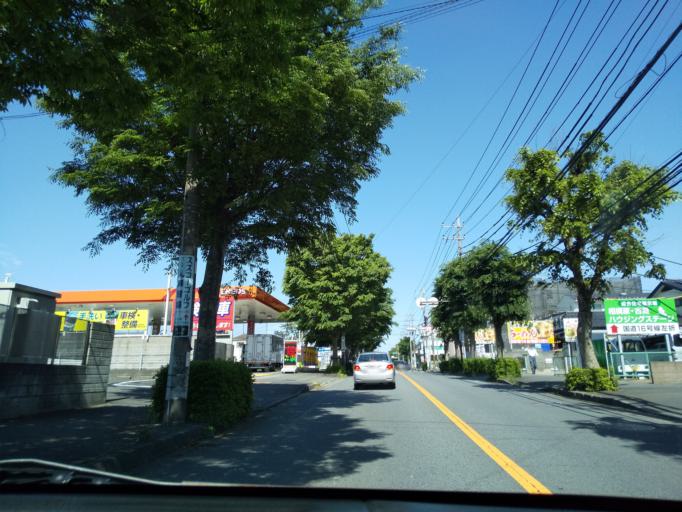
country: JP
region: Kanagawa
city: Zama
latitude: 35.5373
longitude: 139.3984
